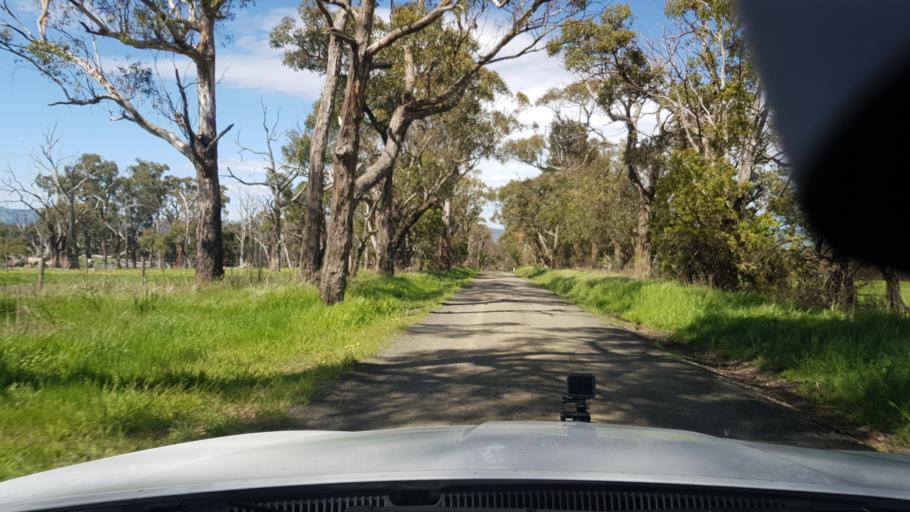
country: AU
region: Victoria
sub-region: Latrobe
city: Moe
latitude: -38.1597
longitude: 146.1357
